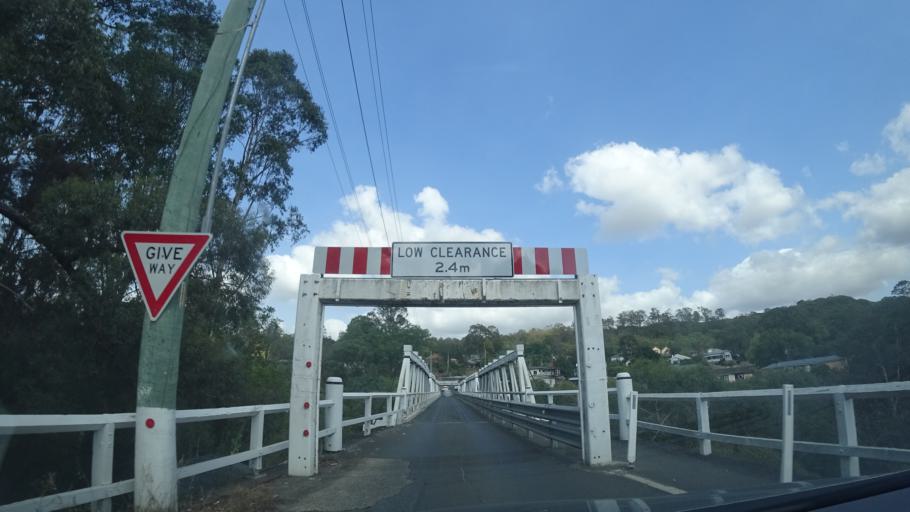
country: AU
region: New South Wales
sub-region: Wollondilly
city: Picton
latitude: -34.1801
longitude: 150.6115
